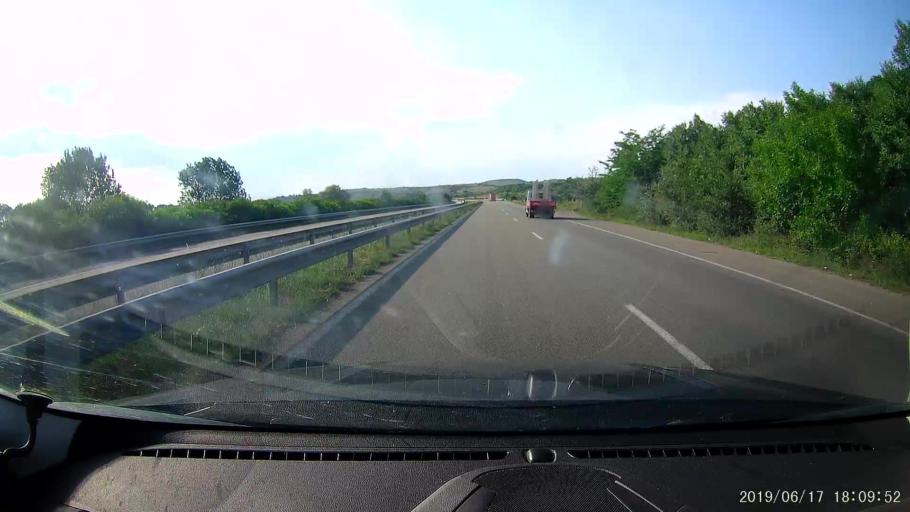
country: BG
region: Khaskovo
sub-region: Obshtina Lyubimets
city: Lyubimets
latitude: 41.8664
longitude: 26.0854
